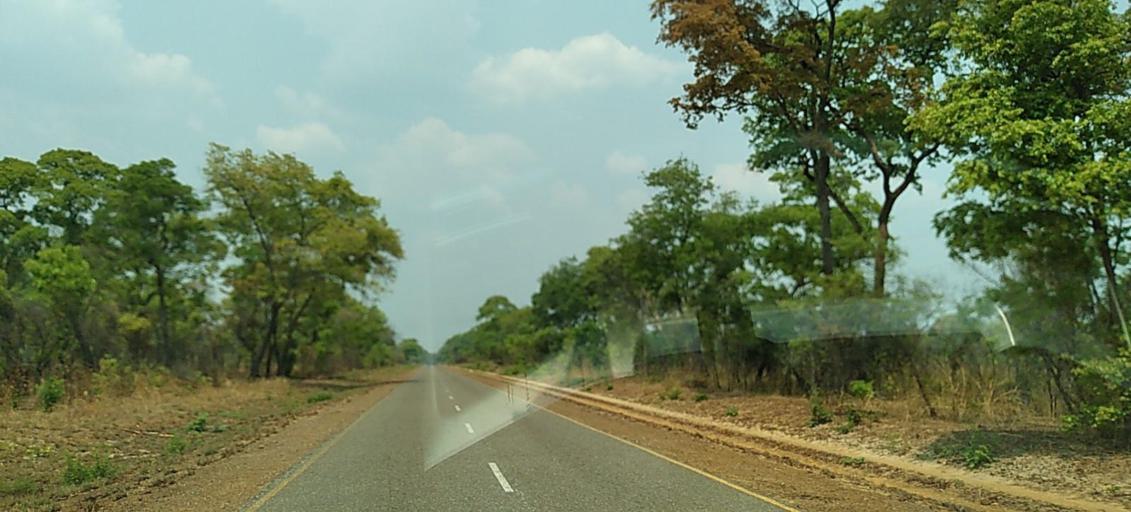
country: ZM
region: North-Western
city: Zambezi
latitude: -13.5571
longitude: 23.1950
